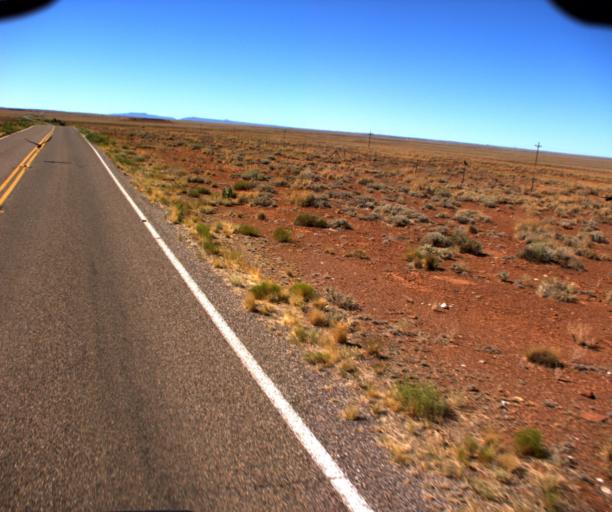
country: US
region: Arizona
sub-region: Coconino County
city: LeChee
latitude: 35.2393
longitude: -110.9598
